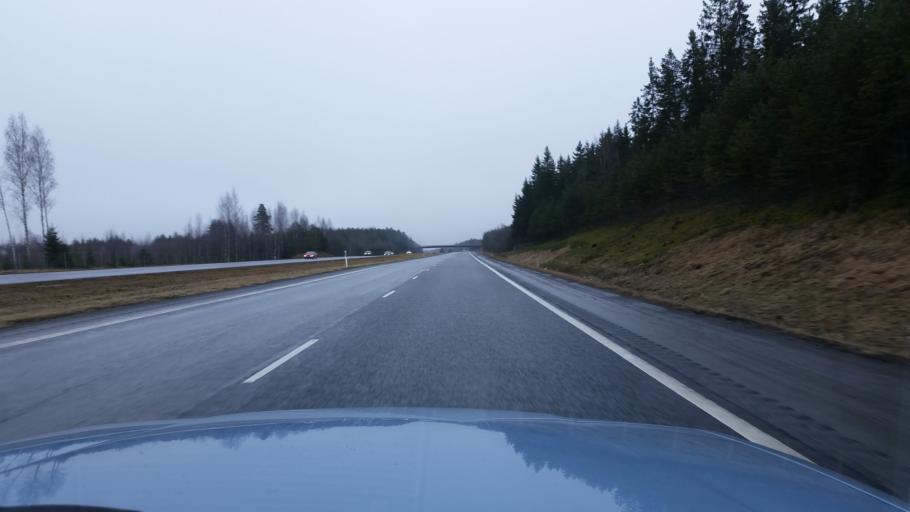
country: FI
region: Haeme
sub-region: Haemeenlinna
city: Kalvola
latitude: 61.1192
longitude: 24.1269
